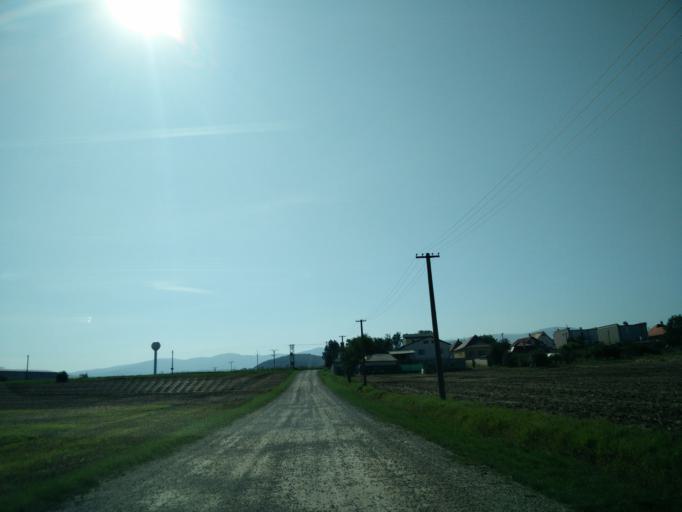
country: SK
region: Nitriansky
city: Banovce nad Bebravou
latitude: 48.5443
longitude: 18.2098
